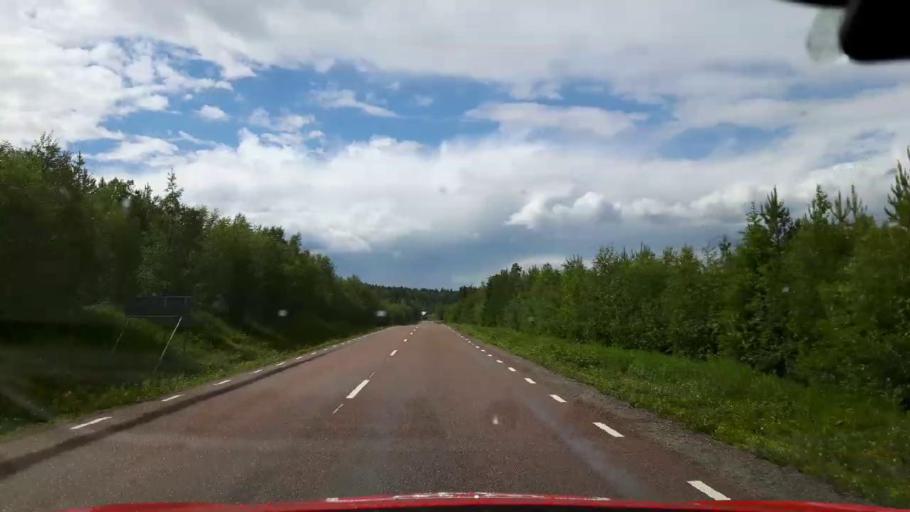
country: SE
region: Jaemtland
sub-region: Krokoms Kommun
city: Valla
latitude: 63.9009
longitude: 14.2324
